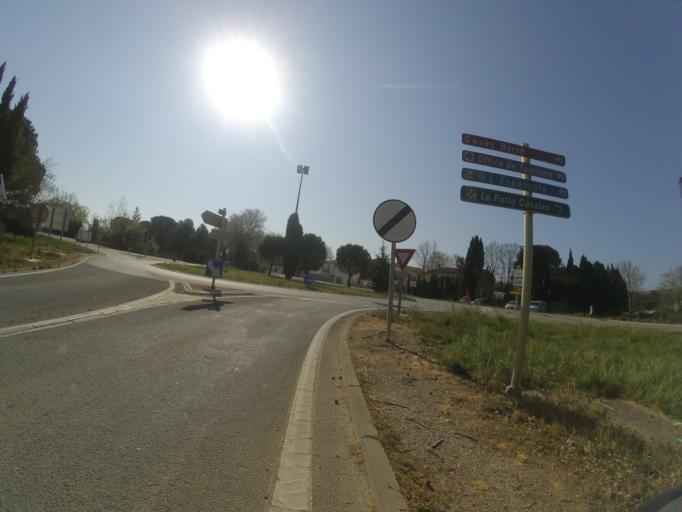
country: FR
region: Languedoc-Roussillon
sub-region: Departement des Pyrenees-Orientales
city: Thuir
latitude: 42.6373
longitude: 2.7498
